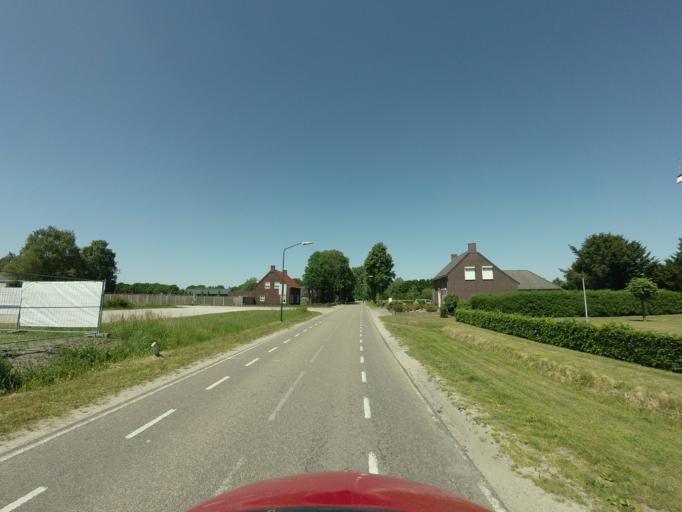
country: NL
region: North Brabant
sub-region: Bergeijk
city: Bergeyk
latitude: 51.2922
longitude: 5.3154
